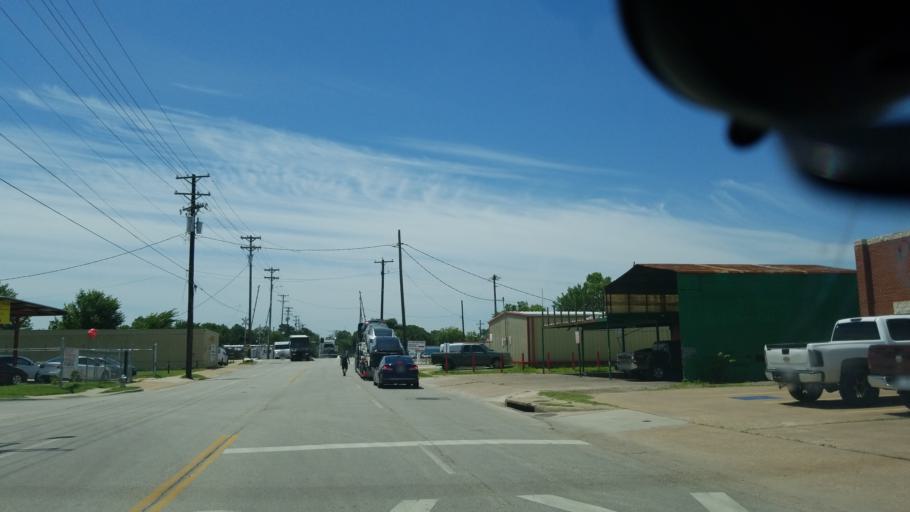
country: US
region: Texas
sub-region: Dallas County
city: Irving
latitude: 32.8158
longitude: -96.9425
